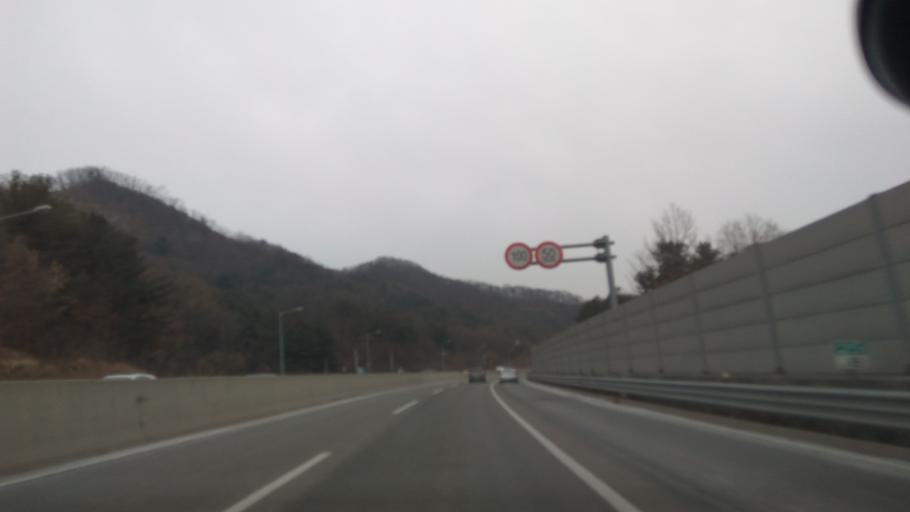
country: KR
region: Gyeonggi-do
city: Cheongpyeong
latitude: 37.6491
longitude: 127.4280
